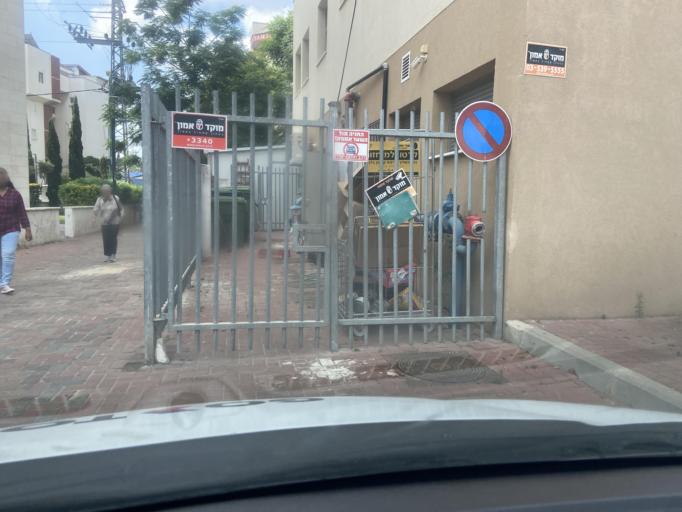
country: IL
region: Central District
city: Yehud
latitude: 32.0370
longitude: 34.8882
